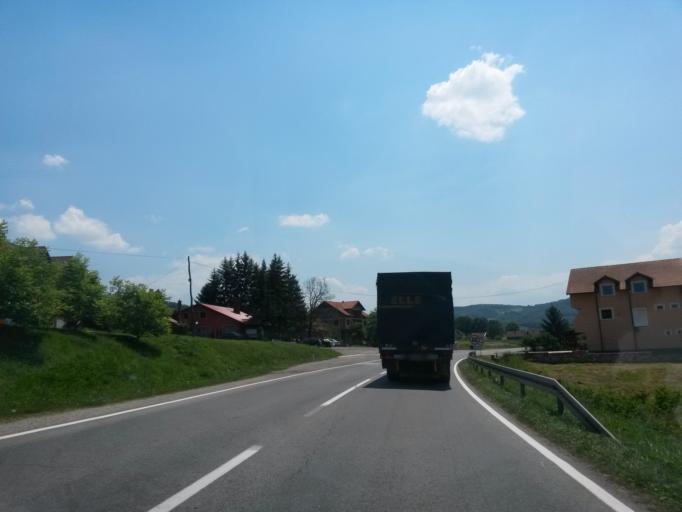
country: BA
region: Federation of Bosnia and Herzegovina
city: Lijesnica
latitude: 44.4924
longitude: 18.0845
